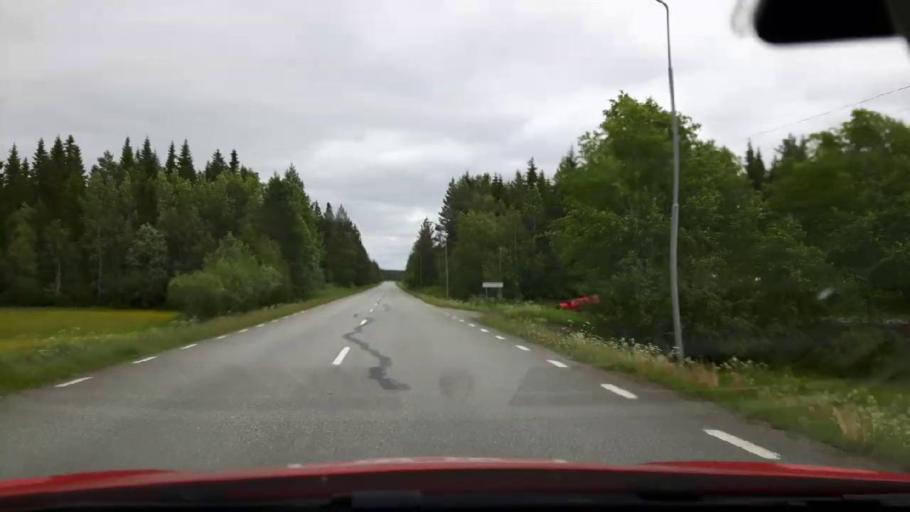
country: SE
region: Jaemtland
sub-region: Stroemsunds Kommun
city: Stroemsund
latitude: 63.5474
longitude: 15.4094
